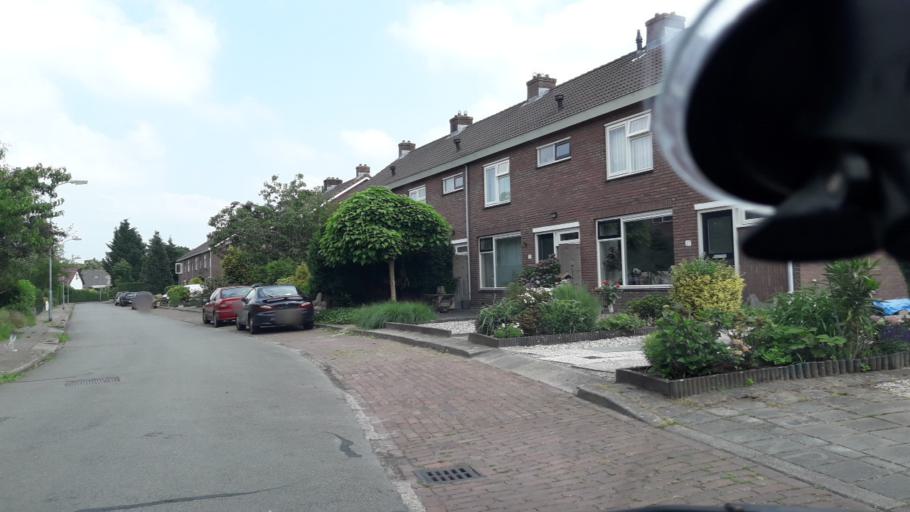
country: NL
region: Gelderland
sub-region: Gemeente Ermelo
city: Ermelo
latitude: 52.2973
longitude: 5.6147
